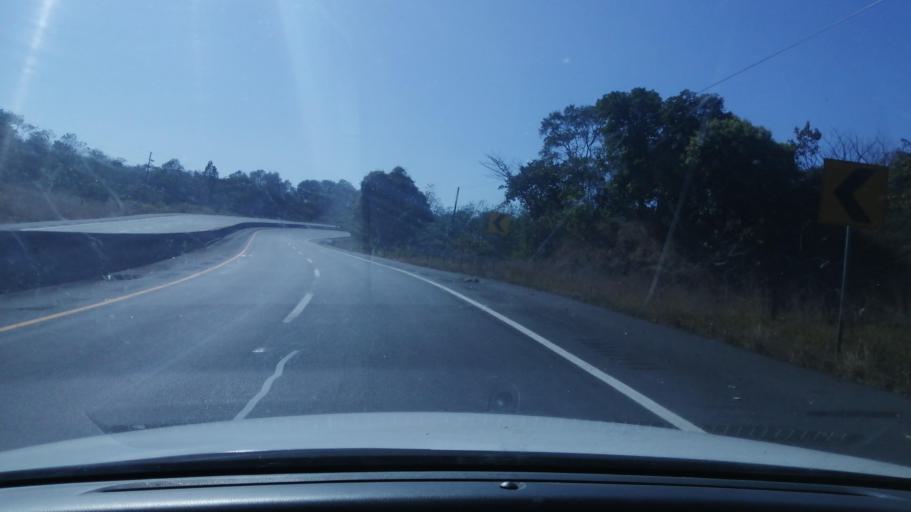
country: PA
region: Chiriqui
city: La Victoria
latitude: 8.3565
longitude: -82.1422
